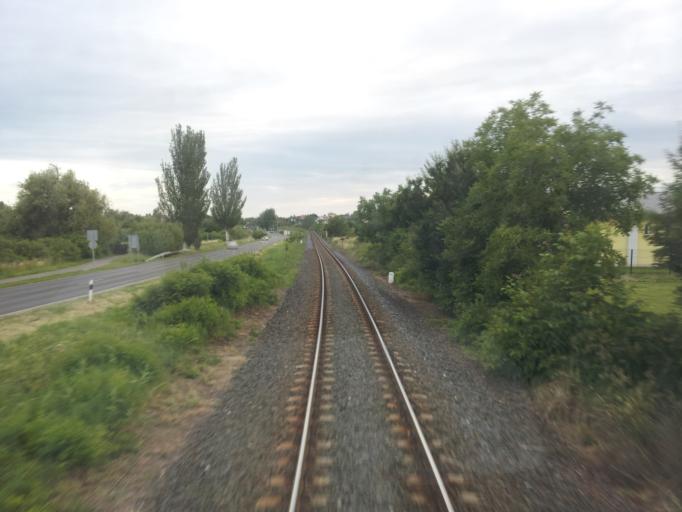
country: HU
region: Veszprem
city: Csopak
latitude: 46.9793
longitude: 17.9411
